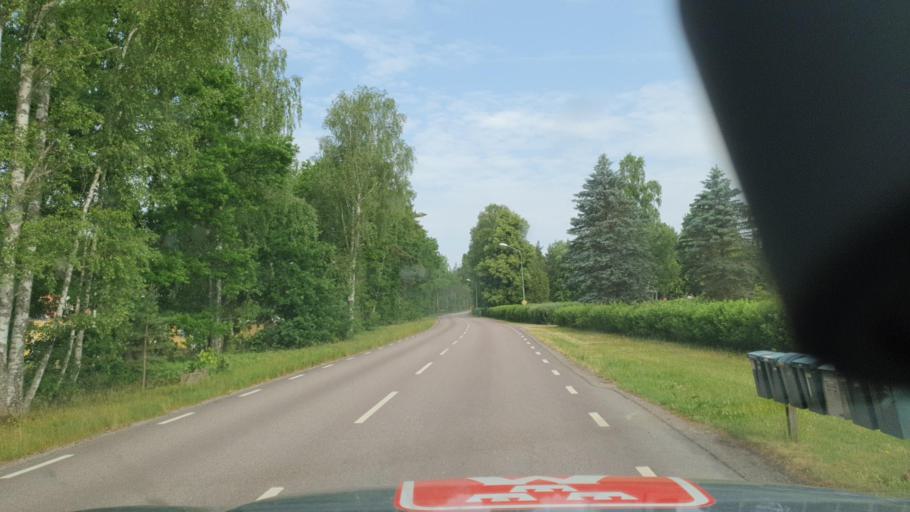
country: SE
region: Kalmar
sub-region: Kalmar Kommun
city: Trekanten
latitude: 56.6255
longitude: 16.0391
